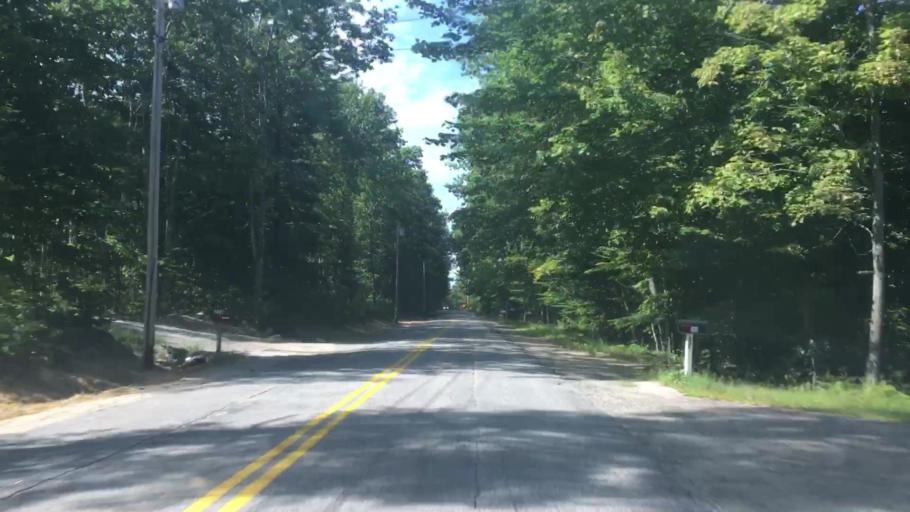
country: US
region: Maine
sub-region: Androscoggin County
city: Poland
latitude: 44.0207
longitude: -70.4244
